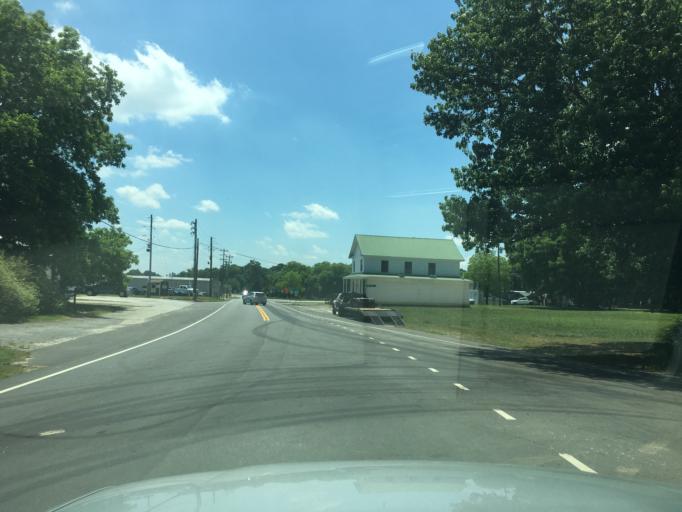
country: US
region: Georgia
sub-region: Hart County
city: Reed Creek
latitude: 34.5122
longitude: -82.9842
